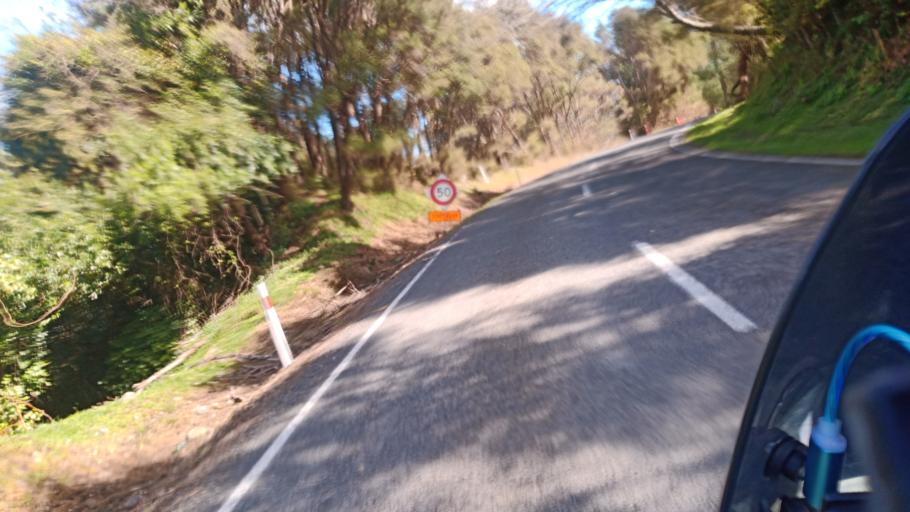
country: NZ
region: Gisborne
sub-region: Gisborne District
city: Gisborne
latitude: -37.8638
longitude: 178.2353
